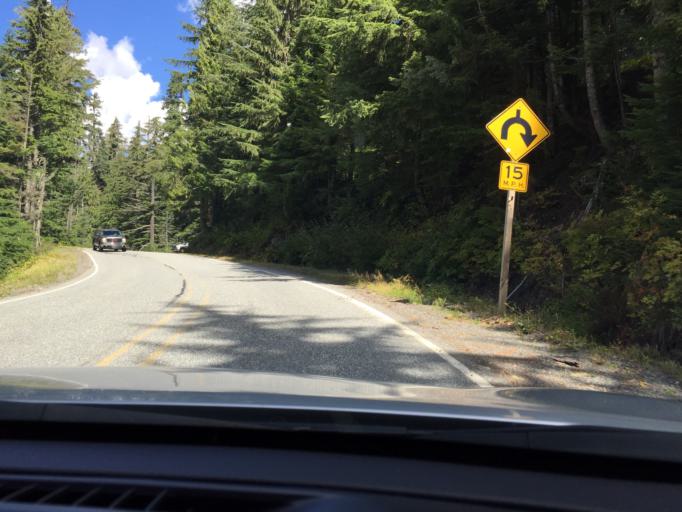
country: CA
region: British Columbia
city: Agassiz
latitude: 48.8656
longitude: -121.6553
